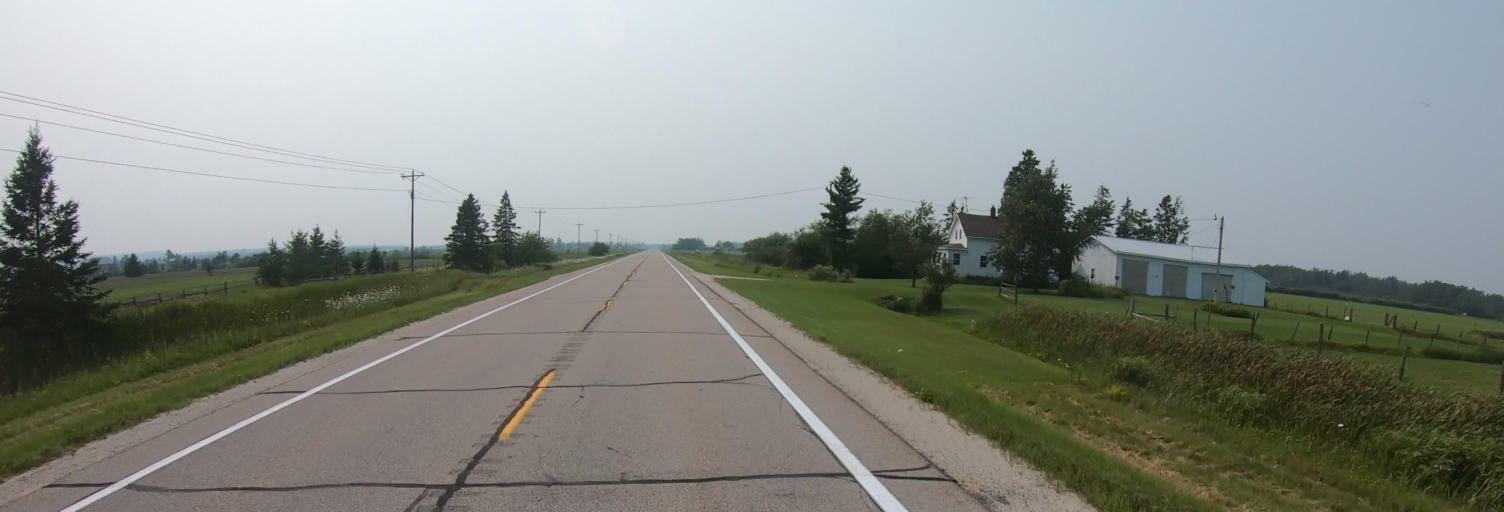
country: US
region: Michigan
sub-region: Chippewa County
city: Sault Ste. Marie
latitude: 46.1291
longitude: -84.2927
